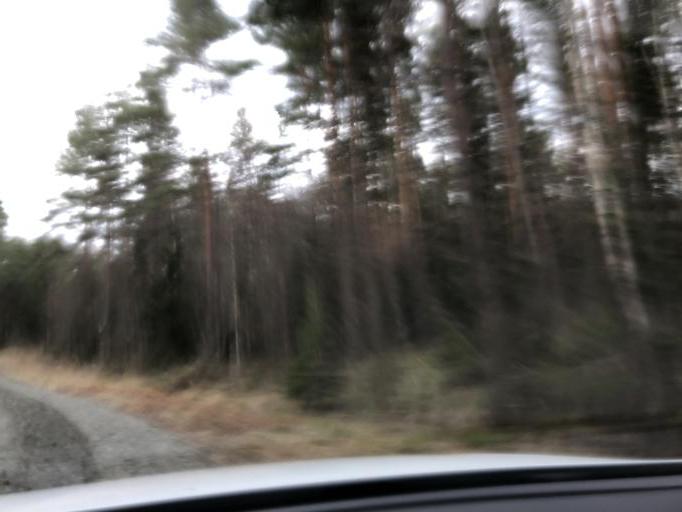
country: SE
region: Uppsala
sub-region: Heby Kommun
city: OEstervala
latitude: 60.3323
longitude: 17.1723
